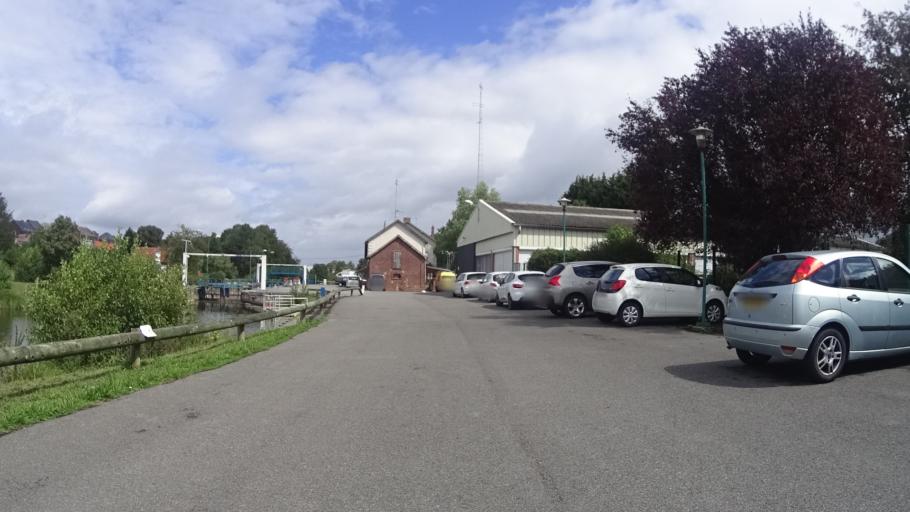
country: FR
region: Nord-Pas-de-Calais
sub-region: Departement du Nord
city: Berlaimont
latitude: 50.2006
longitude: 3.8168
